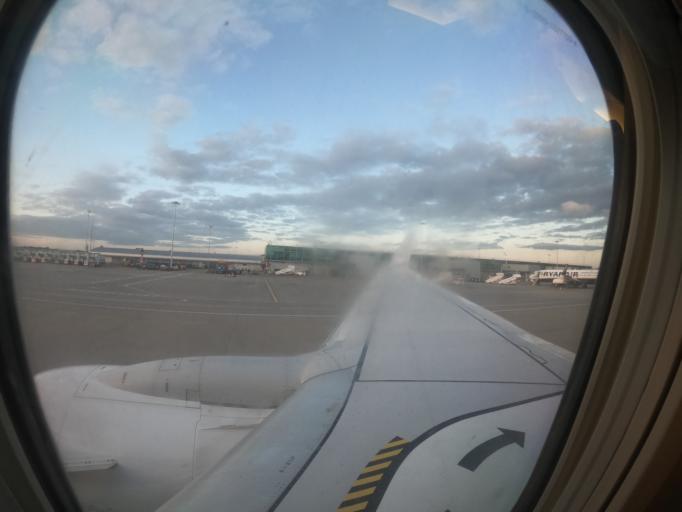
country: GB
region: England
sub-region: Essex
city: Takeley
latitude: 51.8928
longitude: 0.2578
